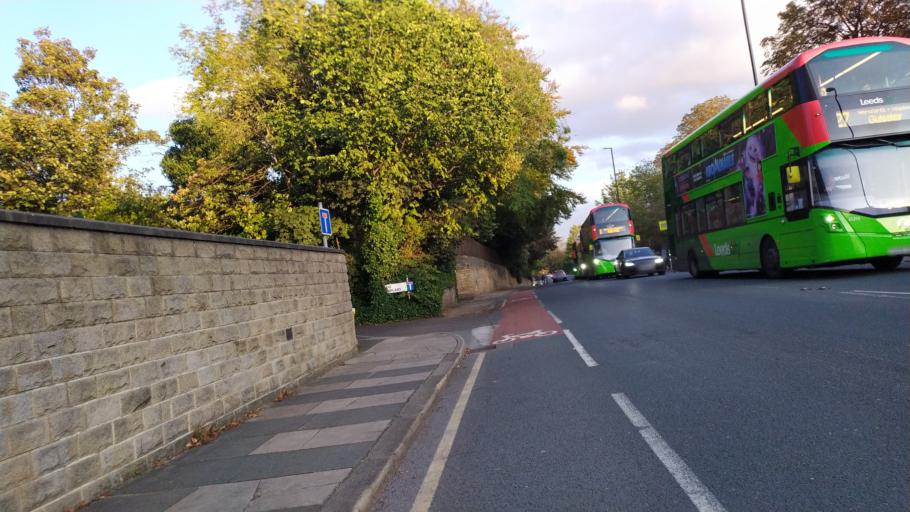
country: GB
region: England
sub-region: City and Borough of Leeds
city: Leeds
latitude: 53.8173
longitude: -1.5709
